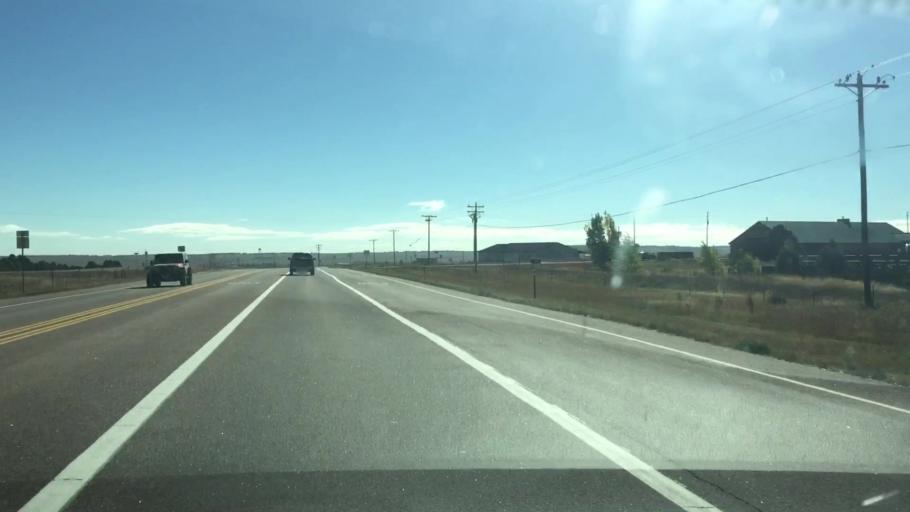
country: US
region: Colorado
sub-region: Elbert County
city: Kiowa
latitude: 39.3550
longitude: -104.5169
